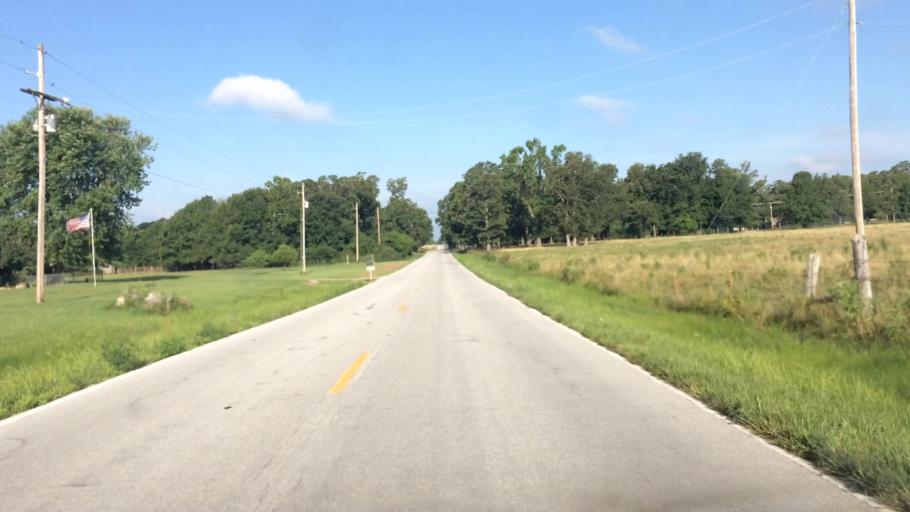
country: US
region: Missouri
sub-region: Greene County
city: Strafford
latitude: 37.2718
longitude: -93.1749
